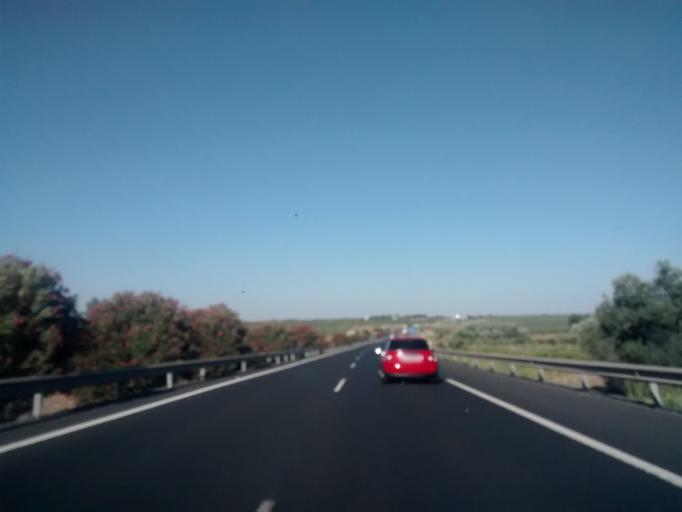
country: ES
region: Andalusia
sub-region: Provincia de Huelva
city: Chucena
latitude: 37.3513
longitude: -6.4107
